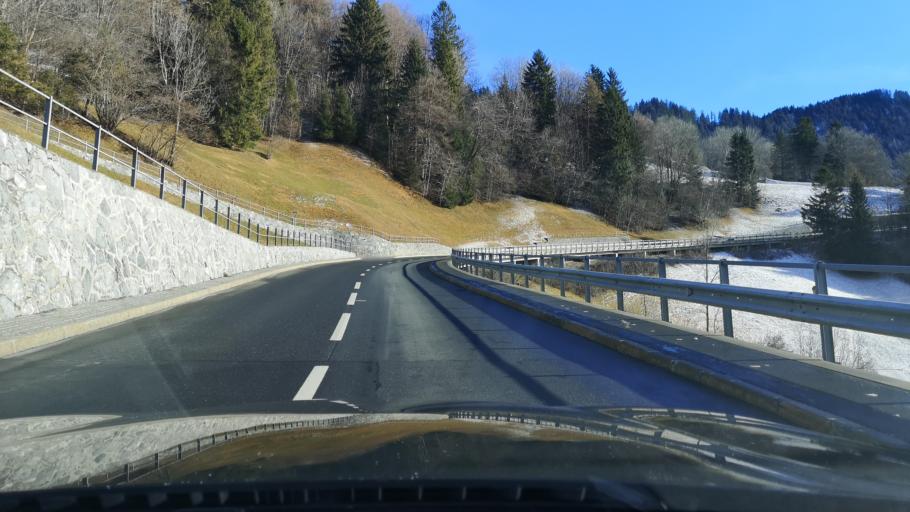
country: LI
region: Triesenberg
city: Triesenberg
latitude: 47.1228
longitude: 9.5493
